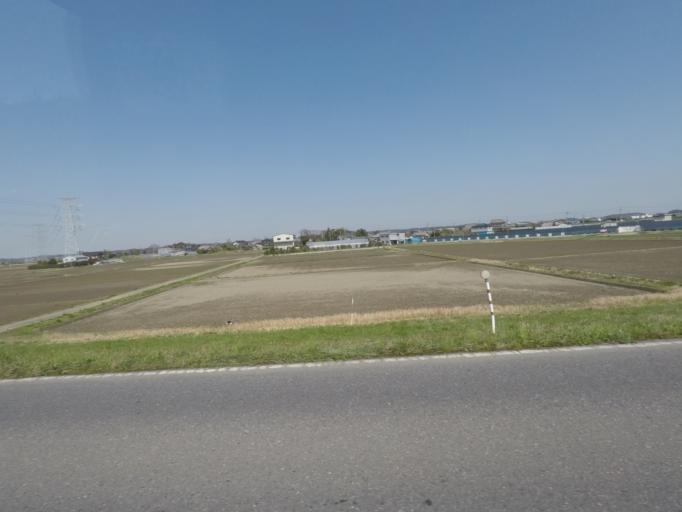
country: JP
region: Ibaraki
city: Inashiki
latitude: 35.9094
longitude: 140.3876
